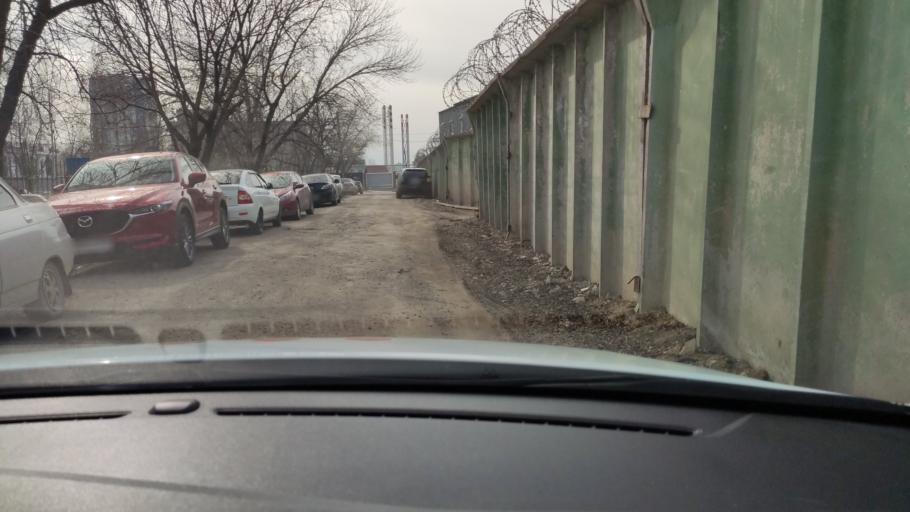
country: RU
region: Tatarstan
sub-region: Gorod Kazan'
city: Kazan
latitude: 55.7491
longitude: 49.1384
